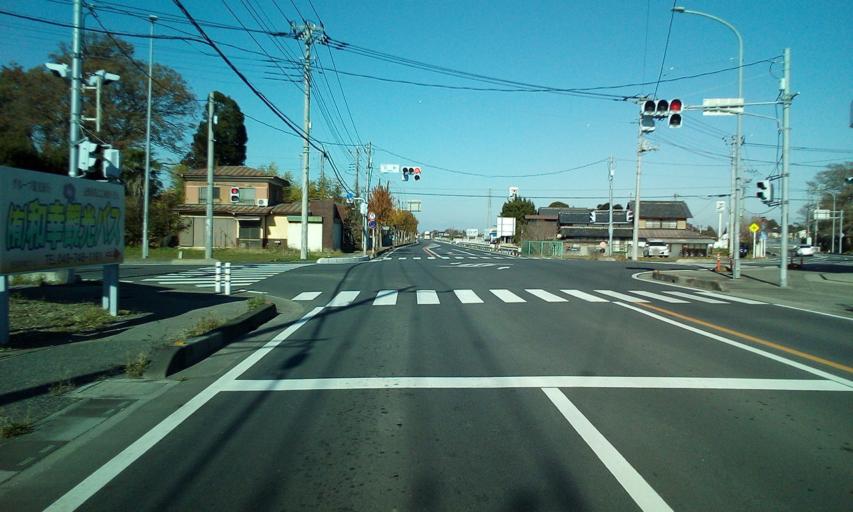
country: JP
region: Saitama
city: Kasukabe
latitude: 36.0099
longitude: 139.7935
